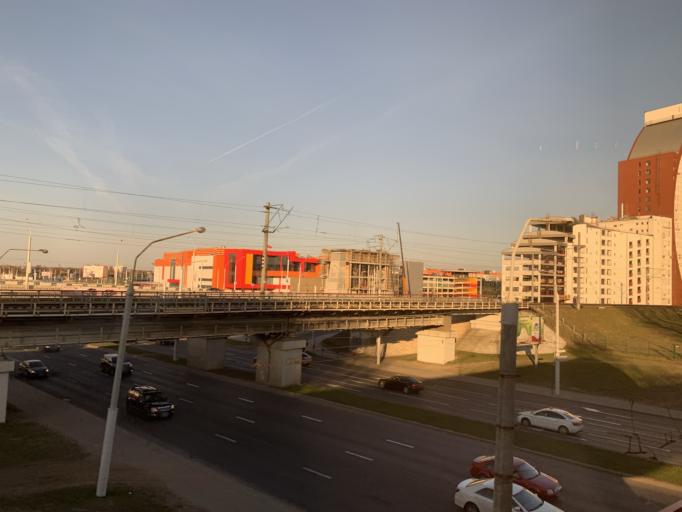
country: BY
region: Minsk
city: Minsk
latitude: 53.9262
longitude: 27.5054
